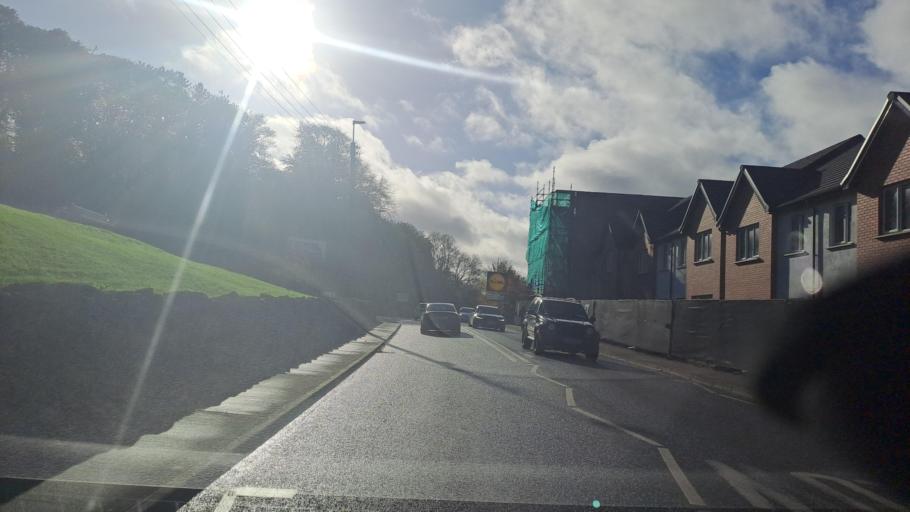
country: IE
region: Ulster
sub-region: County Monaghan
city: Monaghan
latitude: 54.2541
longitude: -6.9653
